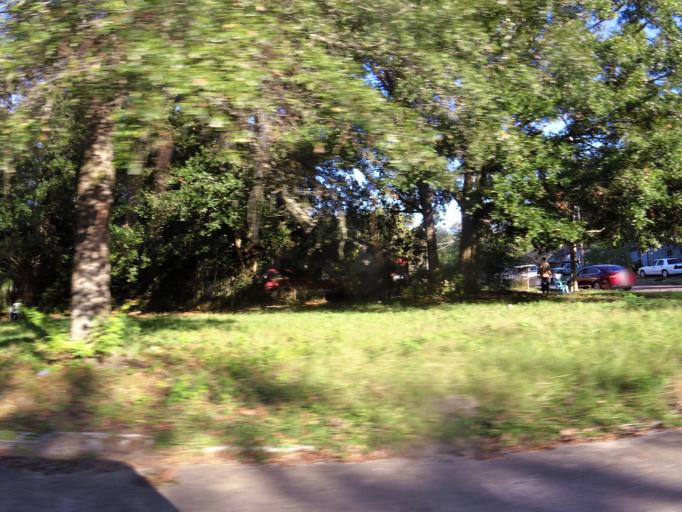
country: US
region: Florida
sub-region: Duval County
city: Jacksonville
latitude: 30.3489
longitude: -81.6832
